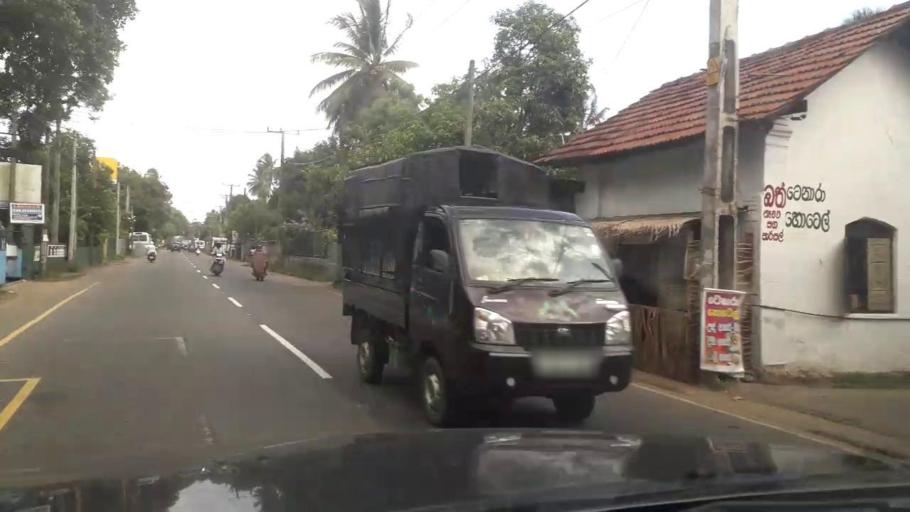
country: LK
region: Western
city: Kalutara
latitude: 6.5391
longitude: 79.9753
